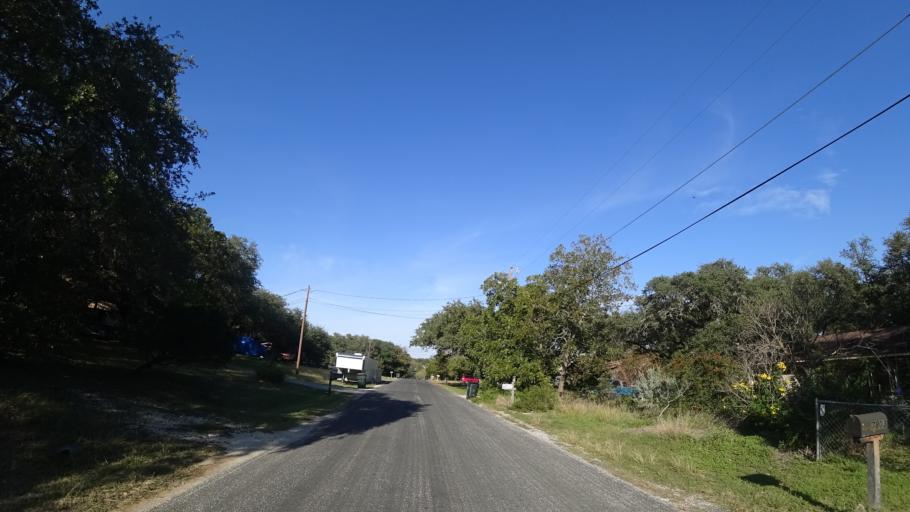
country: US
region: Texas
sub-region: Travis County
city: Barton Creek
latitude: 30.2447
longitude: -97.9162
